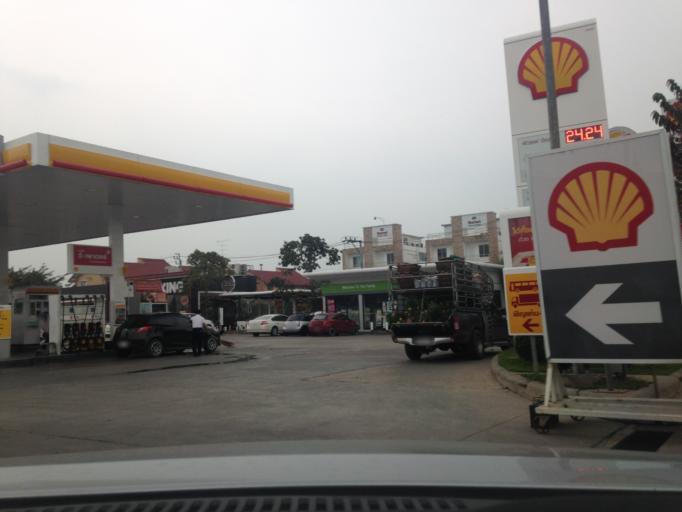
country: TH
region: Bangkok
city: Lat Krabang
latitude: 13.7417
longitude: 100.7466
